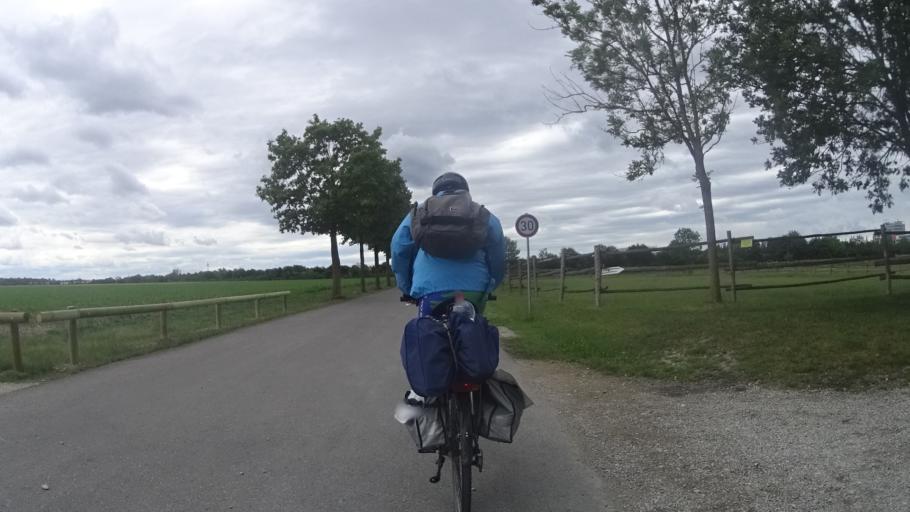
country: DE
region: Bavaria
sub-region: Upper Bavaria
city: Unterschleissheim
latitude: 48.2882
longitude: 11.5938
